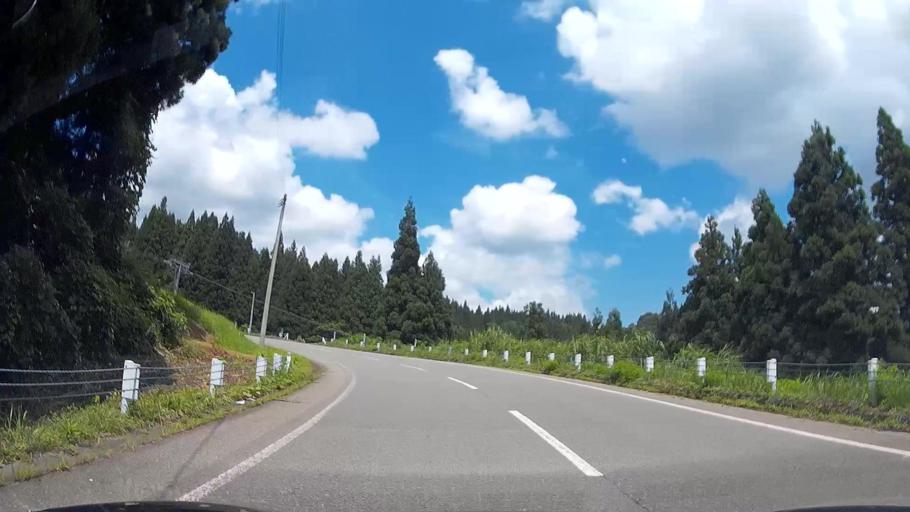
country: JP
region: Niigata
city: Shiozawa
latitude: 37.0242
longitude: 138.8045
